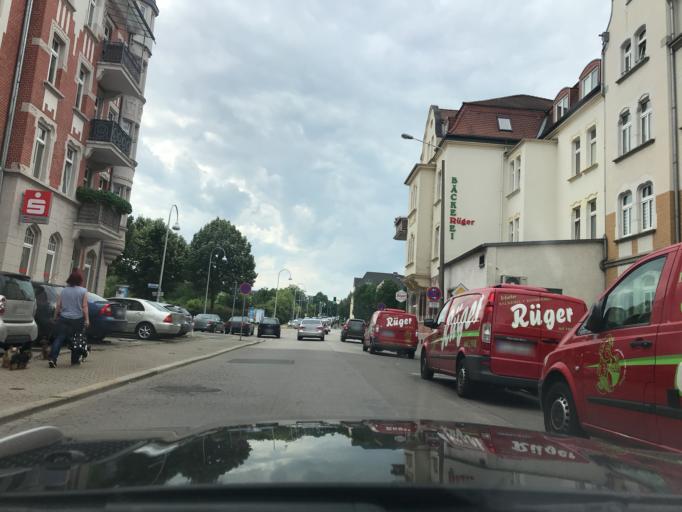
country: DE
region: Thuringia
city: Erfurt
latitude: 50.9821
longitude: 11.0151
